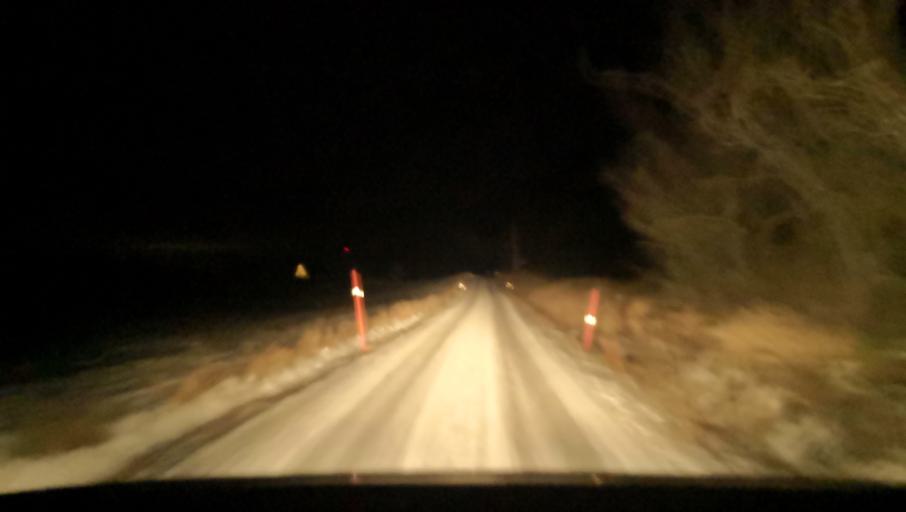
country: SE
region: Uppsala
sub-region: Enkopings Kommun
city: Irsta
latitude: 59.6506
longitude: 16.8657
